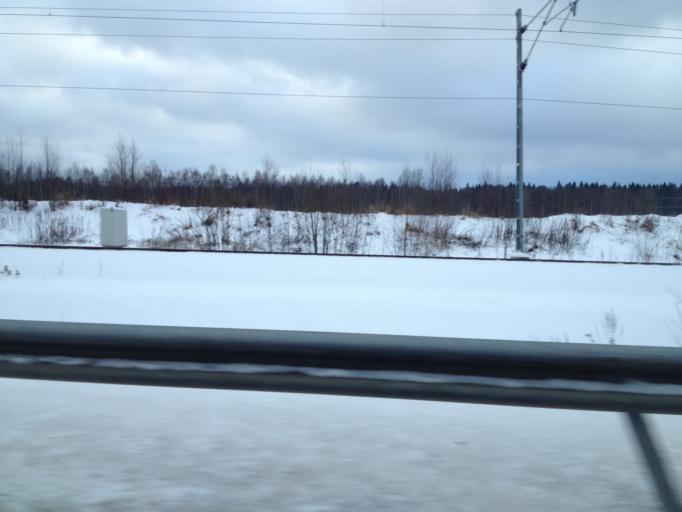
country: FI
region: Uusimaa
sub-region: Helsinki
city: Vantaa
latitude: 60.2404
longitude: 25.1552
